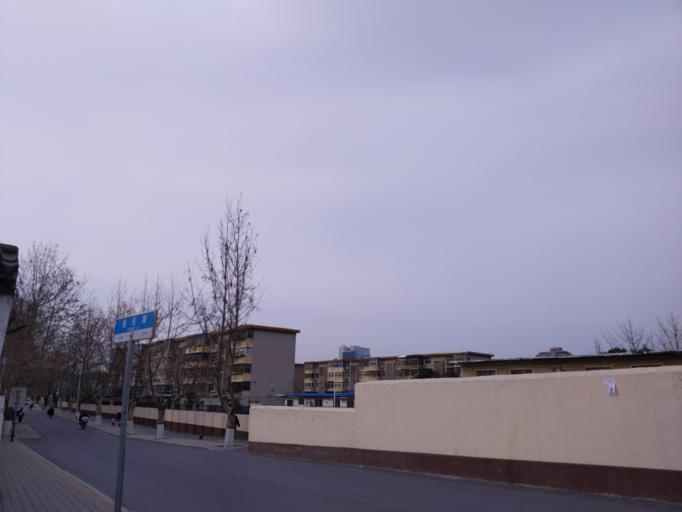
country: CN
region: Henan Sheng
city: Zhongyuanlu
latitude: 35.7592
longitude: 115.0451
